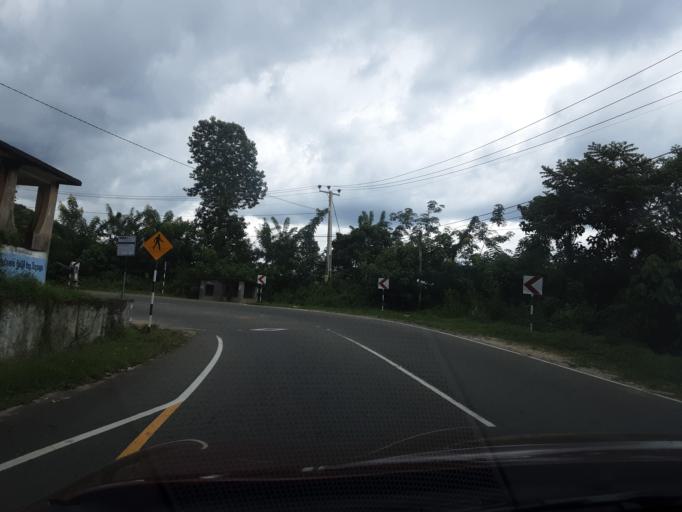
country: LK
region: Uva
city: Monaragala
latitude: 6.9009
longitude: 81.2145
